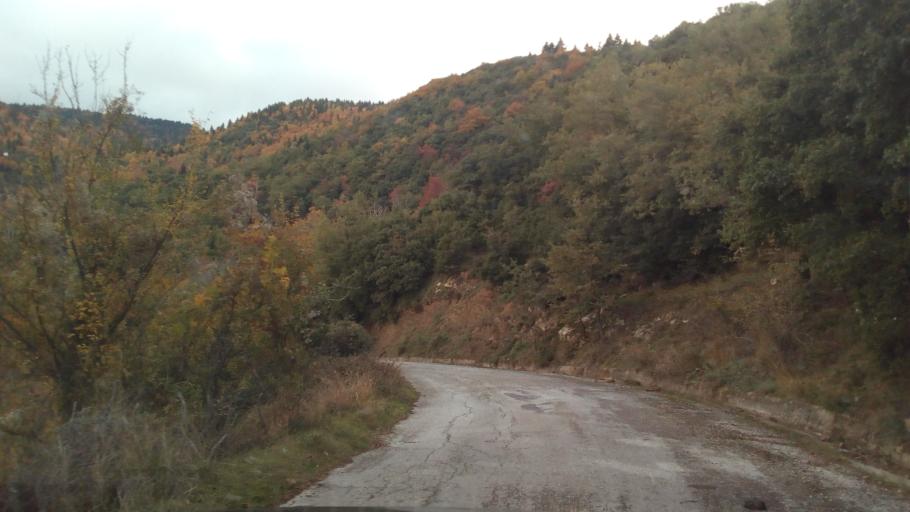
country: GR
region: Central Greece
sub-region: Nomos Fokidos
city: Lidoriki
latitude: 38.5649
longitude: 21.9813
